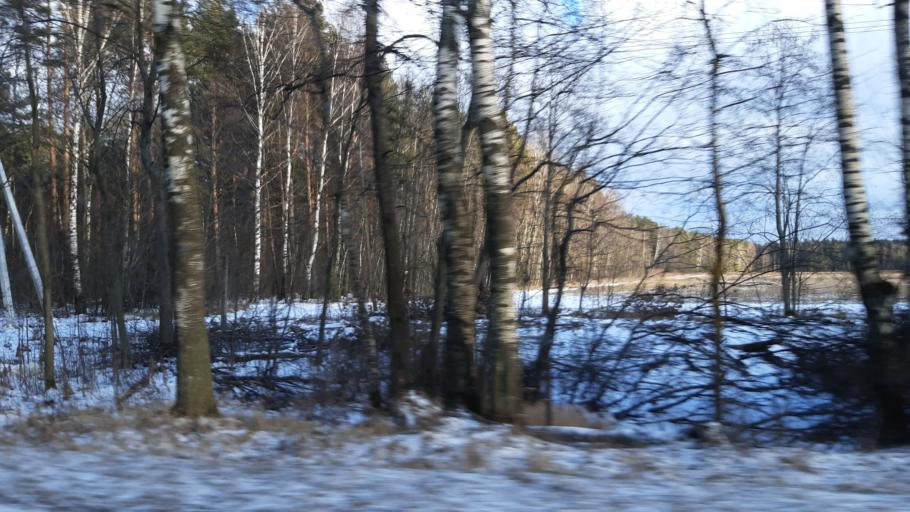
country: RU
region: Moskovskaya
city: Noginsk-9
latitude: 56.0452
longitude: 38.5521
